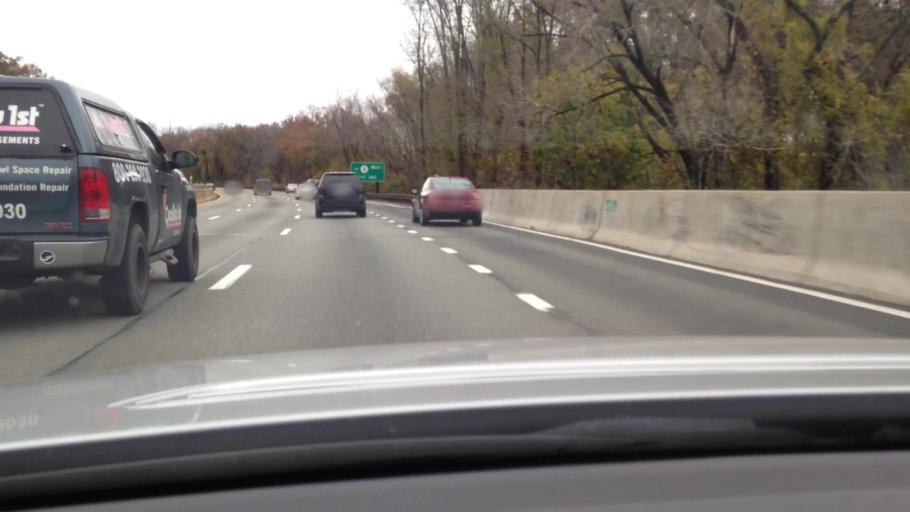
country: US
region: New Jersey
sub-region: Bergen County
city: Saddle Brook
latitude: 40.9116
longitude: -74.0904
